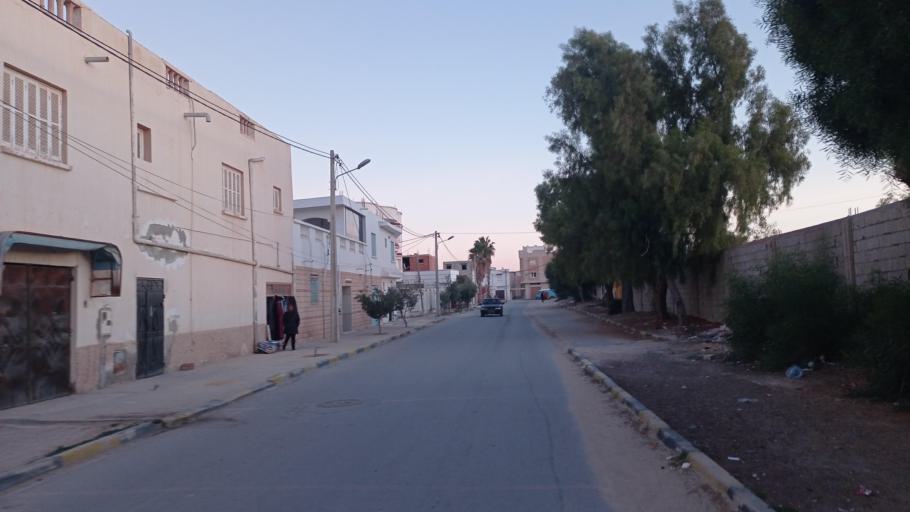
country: TN
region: Qabis
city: Gabes
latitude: 33.8450
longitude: 10.1161
